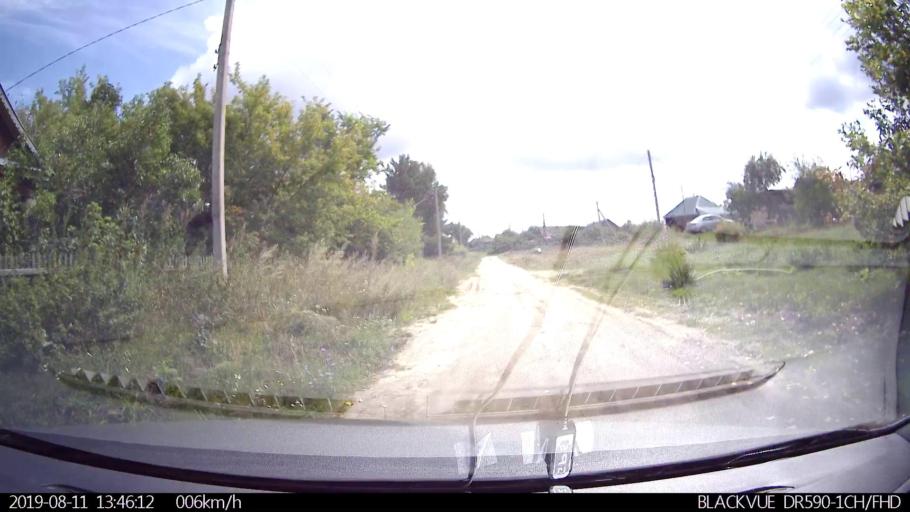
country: RU
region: Ulyanovsk
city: Ignatovka
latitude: 53.8515
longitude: 47.5751
